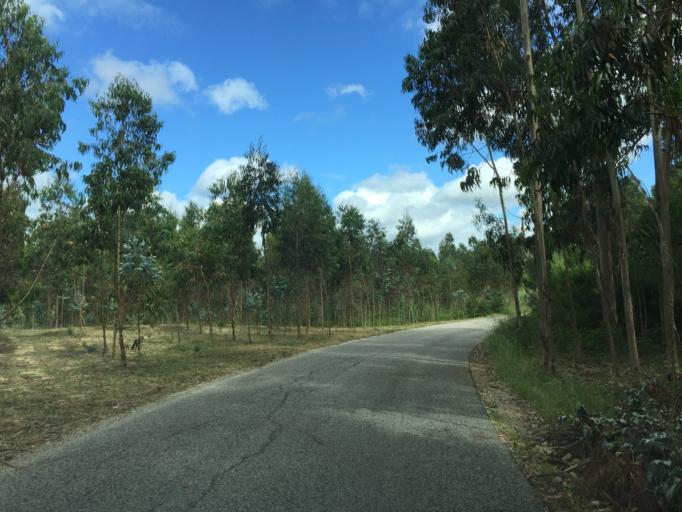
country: PT
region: Coimbra
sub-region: Figueira da Foz
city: Tavarede
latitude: 40.2107
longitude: -8.8316
